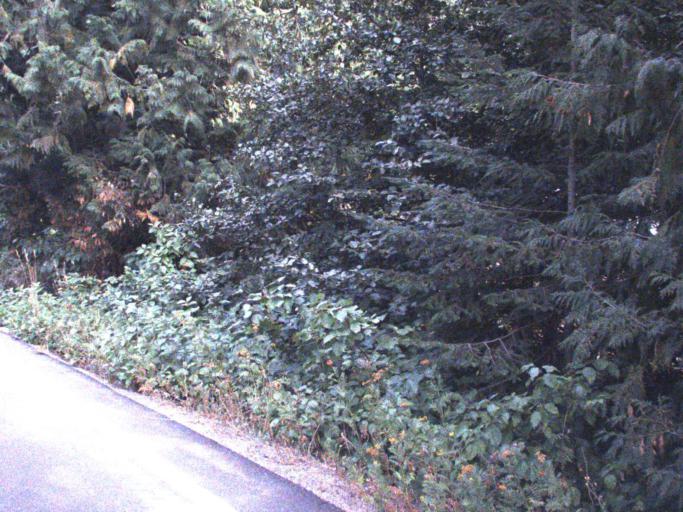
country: US
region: Washington
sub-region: Spokane County
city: Otis Orchards-East Farms
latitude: 47.8703
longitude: -117.1566
